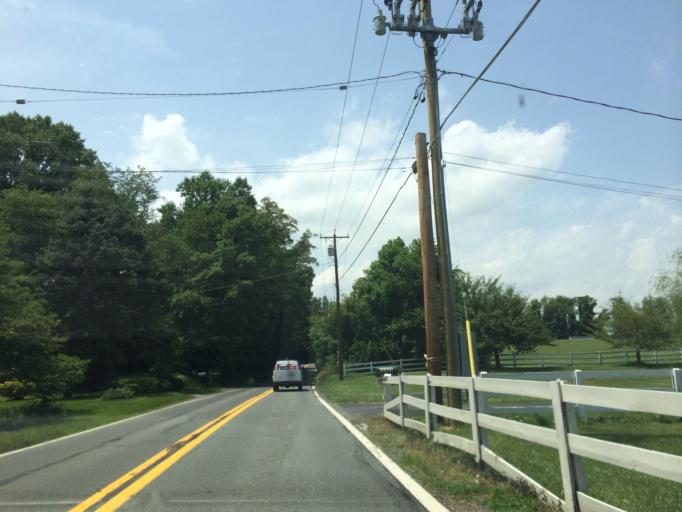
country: US
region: Maryland
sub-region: Montgomery County
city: Ashton-Sandy Spring
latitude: 39.2051
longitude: -77.0326
